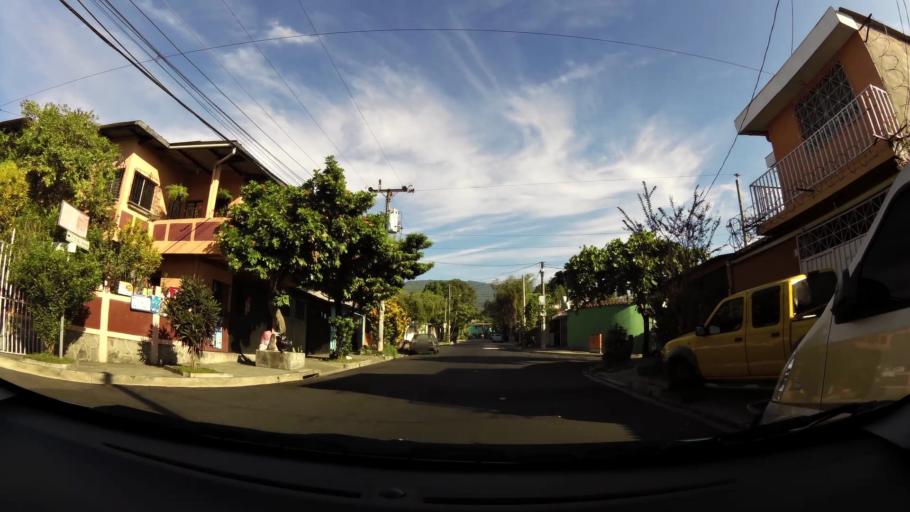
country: SV
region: La Libertad
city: Santa Tecla
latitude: 13.6808
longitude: -89.2855
